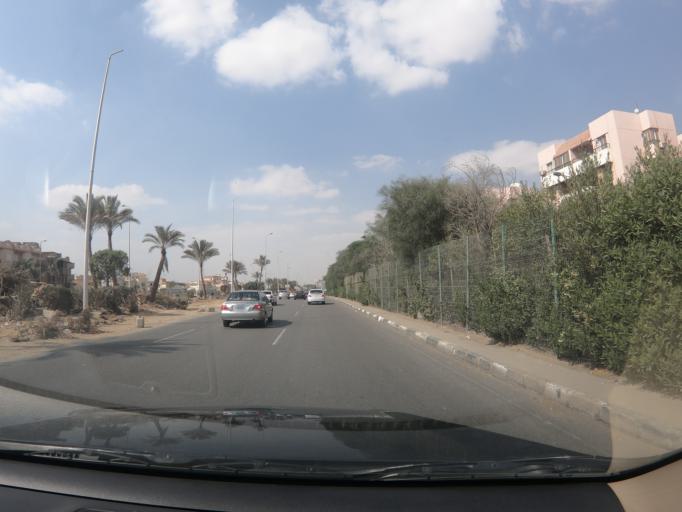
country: EG
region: Muhafazat al Qalyubiyah
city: Al Khankah
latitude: 30.0626
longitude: 31.4752
